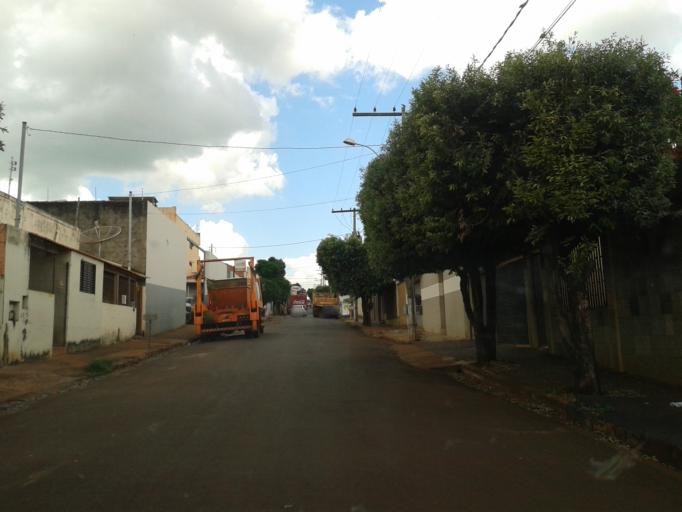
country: BR
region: Minas Gerais
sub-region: Capinopolis
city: Capinopolis
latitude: -18.6820
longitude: -49.5748
